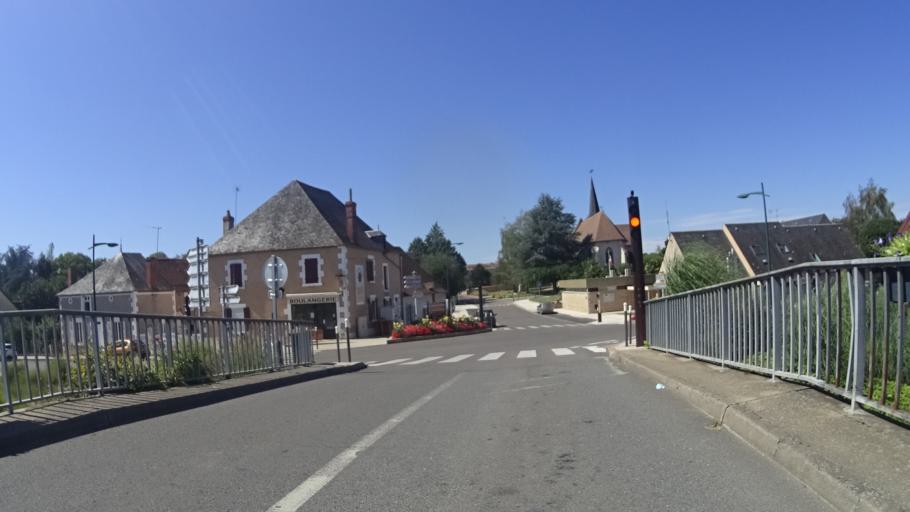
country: FR
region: Centre
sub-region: Departement du Cher
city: Belleville-sur-Loire
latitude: 47.5073
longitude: 2.8525
